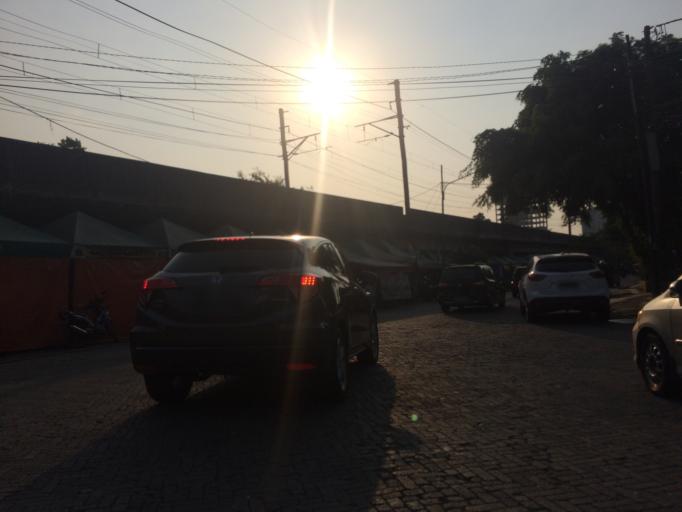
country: ID
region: Jakarta Raya
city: Jakarta
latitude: -6.2033
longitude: 106.8451
